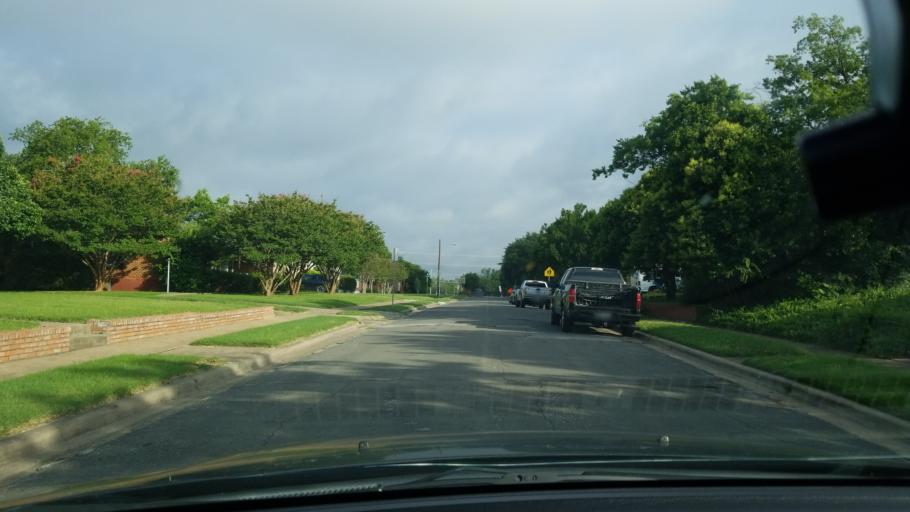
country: US
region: Texas
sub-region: Dallas County
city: Highland Park
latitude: 32.8245
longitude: -96.6909
